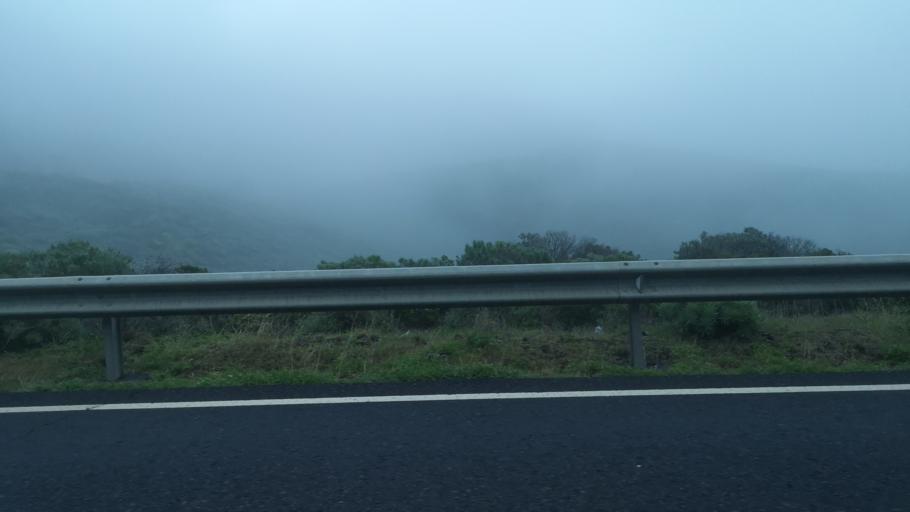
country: ES
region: Canary Islands
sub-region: Provincia de Santa Cruz de Tenerife
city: Alajero
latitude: 28.0802
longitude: -17.2018
